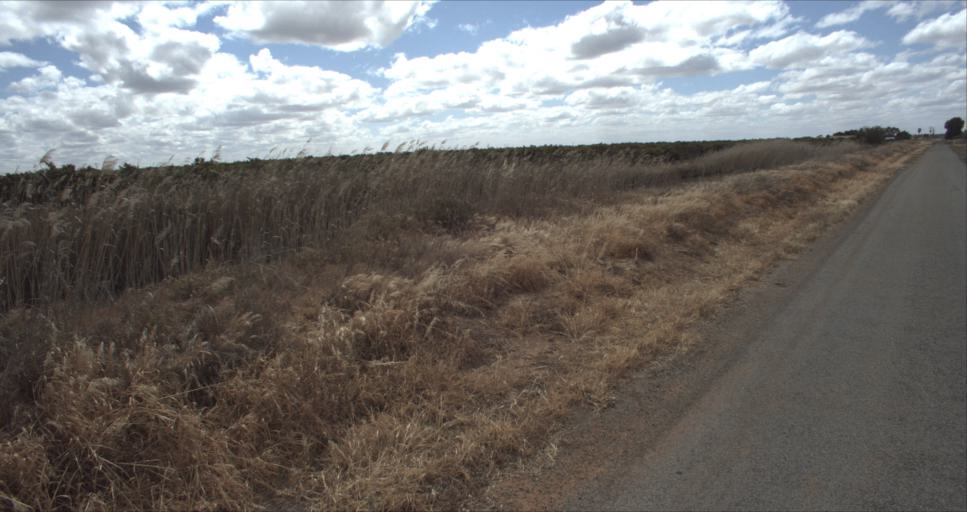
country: AU
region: New South Wales
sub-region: Leeton
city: Leeton
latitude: -34.5887
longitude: 146.3908
